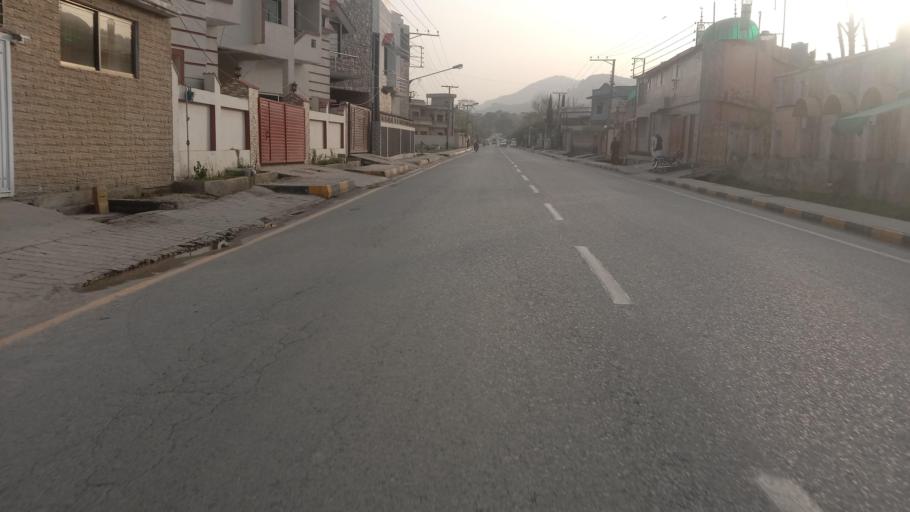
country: PK
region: Khyber Pakhtunkhwa
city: Abbottabad
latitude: 34.1693
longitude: 73.2309
